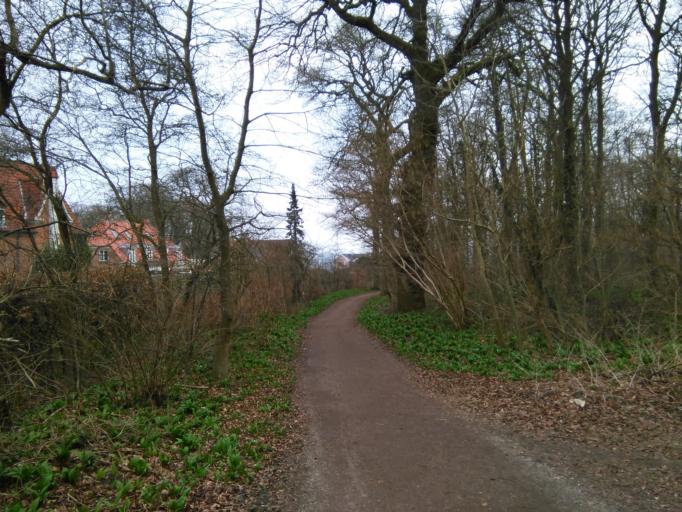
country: DK
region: Central Jutland
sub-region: Arhus Kommune
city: Arhus
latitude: 56.1817
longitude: 10.2295
